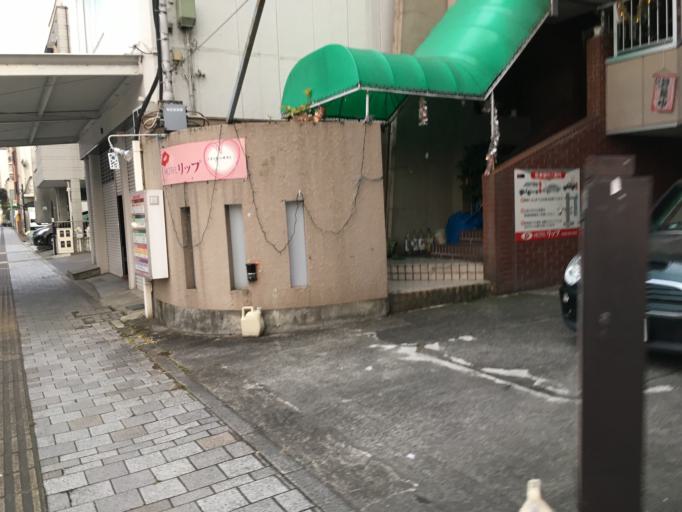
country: JP
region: Tochigi
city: Utsunomiya-shi
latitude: 36.5576
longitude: 139.8912
